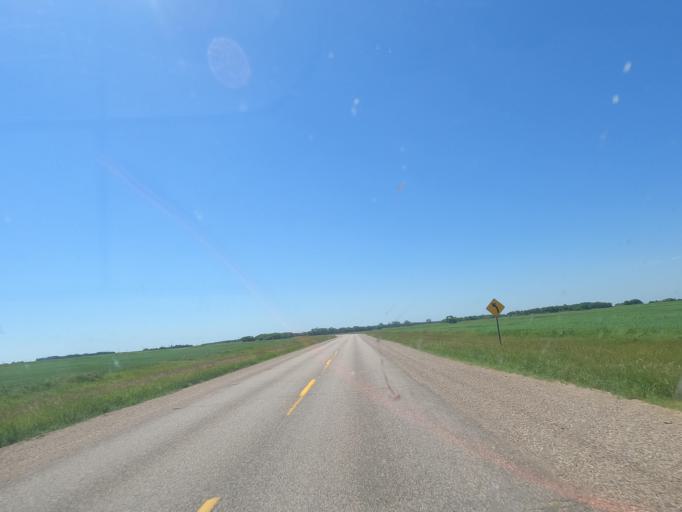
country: CA
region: Manitoba
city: Souris
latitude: 49.6170
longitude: -100.5254
